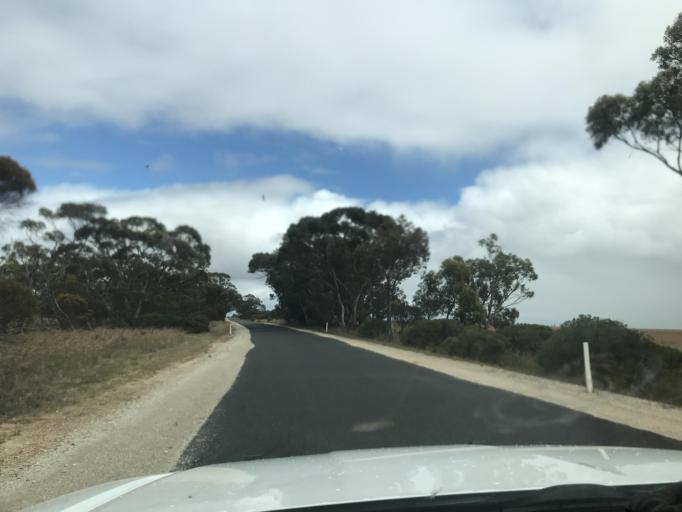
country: AU
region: South Australia
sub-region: Tatiara
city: Bordertown
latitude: -36.1397
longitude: 141.2208
